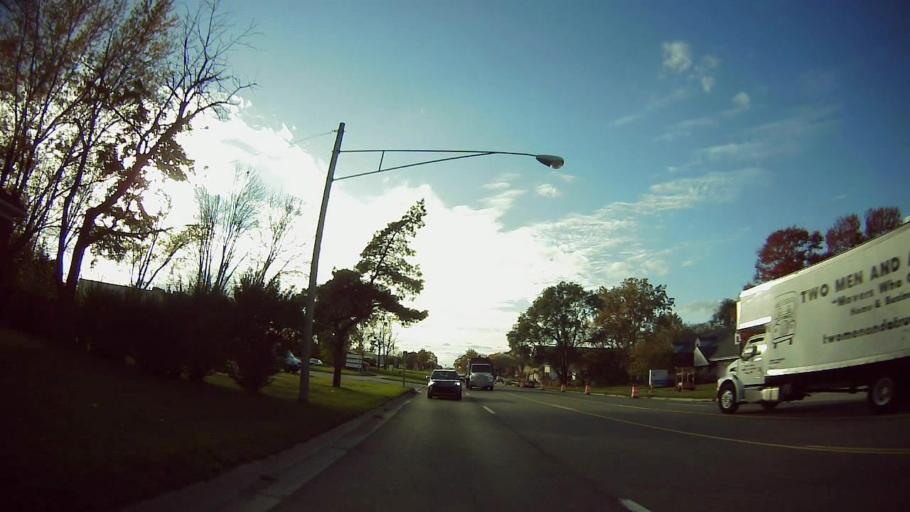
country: US
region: Michigan
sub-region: Oakland County
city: Clawson
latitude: 42.5483
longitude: -83.1354
